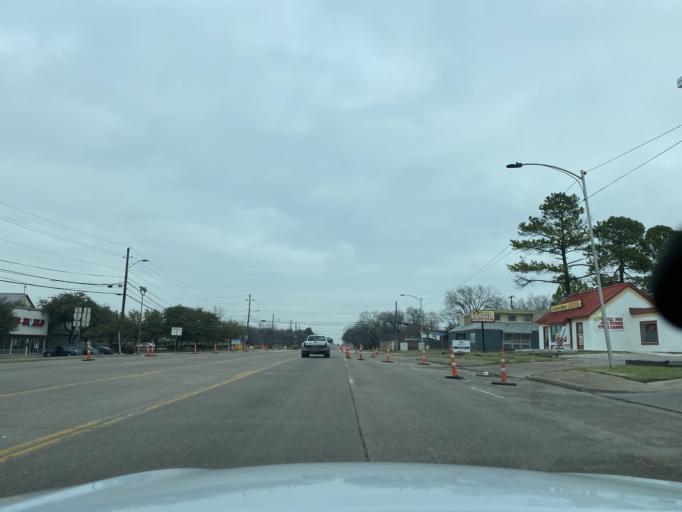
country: US
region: Texas
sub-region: Tarrant County
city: Arlington
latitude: 32.7090
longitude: -97.0975
